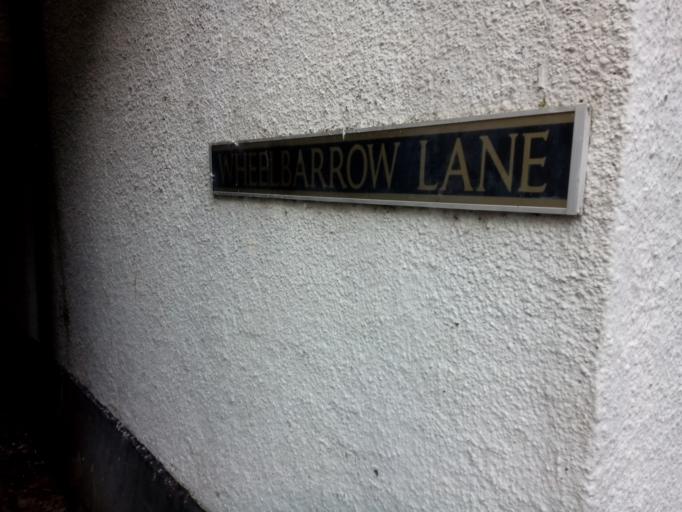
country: GB
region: England
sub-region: Cornwall
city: Helston
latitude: 50.1013
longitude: -5.2748
